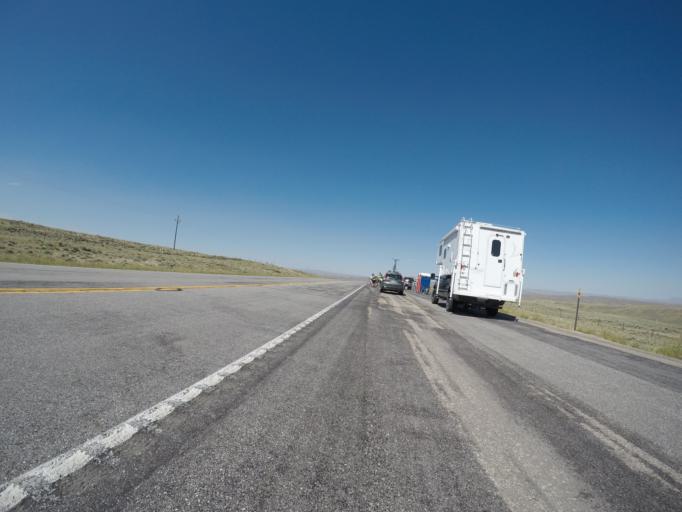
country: US
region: Wyoming
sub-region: Carbon County
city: Saratoga
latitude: 41.7944
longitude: -106.7396
